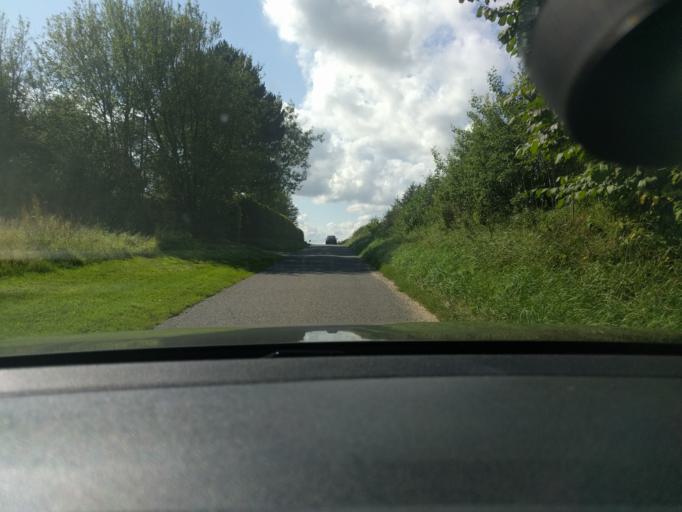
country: DK
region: Central Jutland
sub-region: Viborg Kommune
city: Bjerringbro
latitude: 56.4628
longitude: 9.5930
